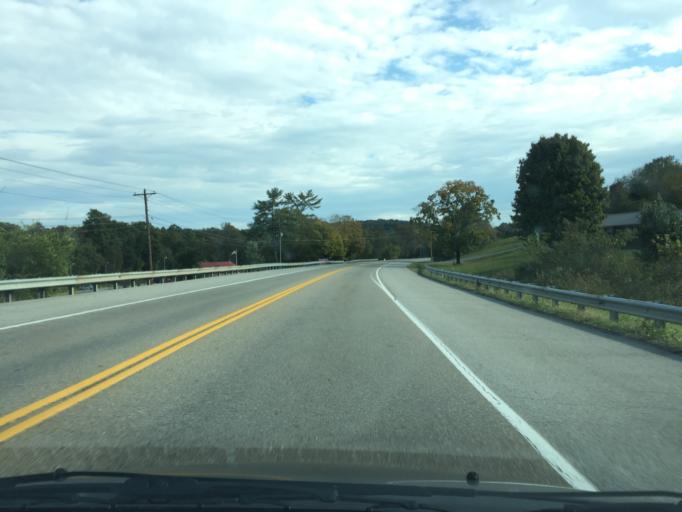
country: US
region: Tennessee
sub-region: Loudon County
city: Loudon
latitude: 35.7294
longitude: -84.3824
